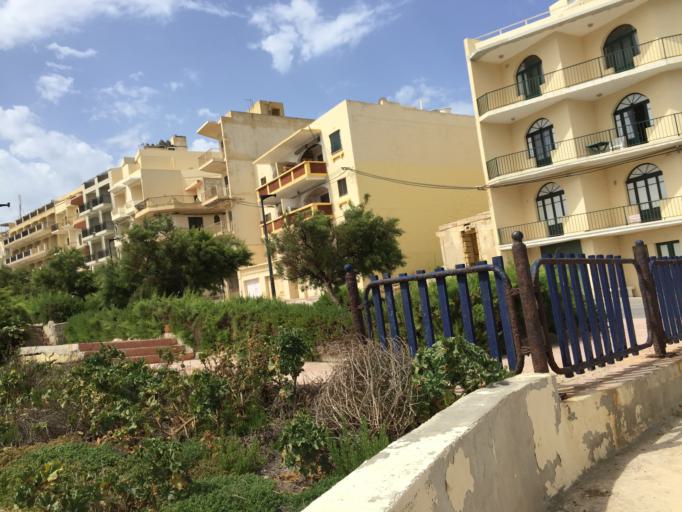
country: MT
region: Iz-Zebbug
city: Zebbug
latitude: 36.0756
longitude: 14.2579
